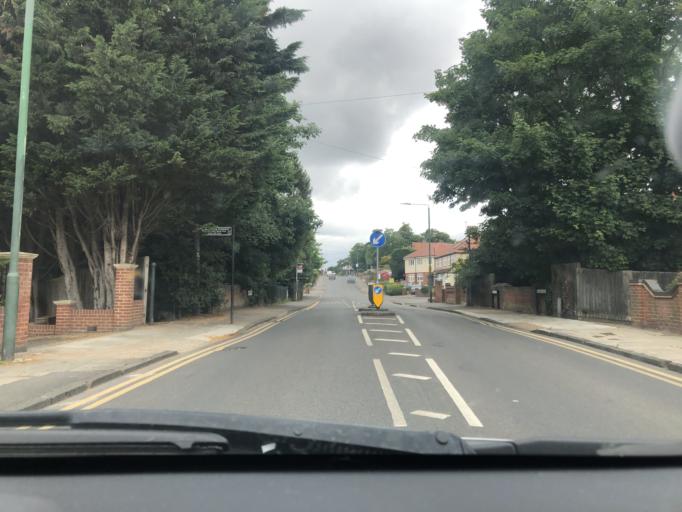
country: GB
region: England
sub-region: Greater London
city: Bexley
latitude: 51.4445
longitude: 0.1358
